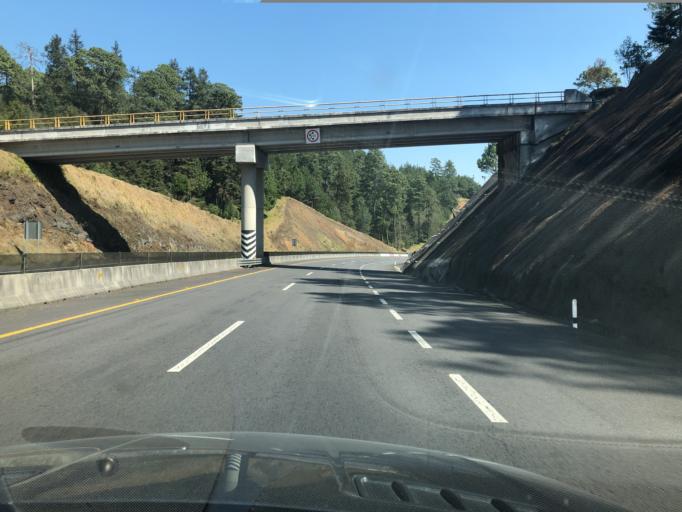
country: MX
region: Veracruz
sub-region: Acajete
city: La Joya
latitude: 19.6228
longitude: -97.0570
